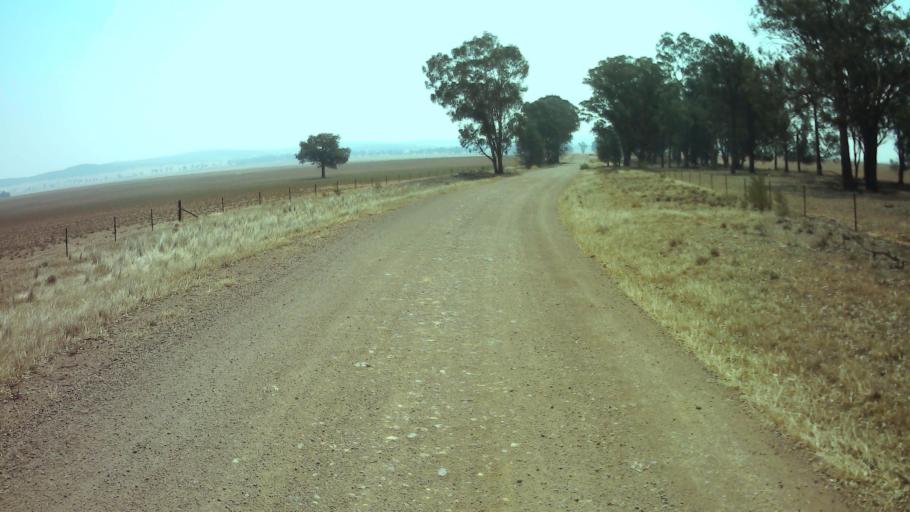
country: AU
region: New South Wales
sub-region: Weddin
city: Grenfell
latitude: -33.6373
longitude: 148.2234
